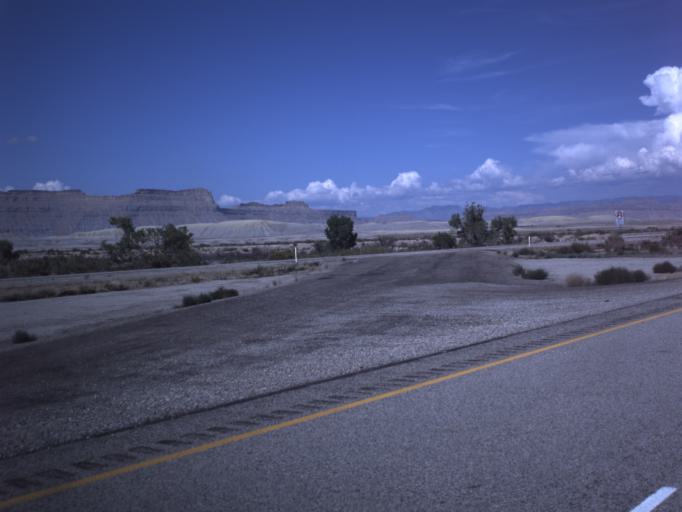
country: US
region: Utah
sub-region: Carbon County
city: East Carbon City
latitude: 38.9768
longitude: -110.2454
